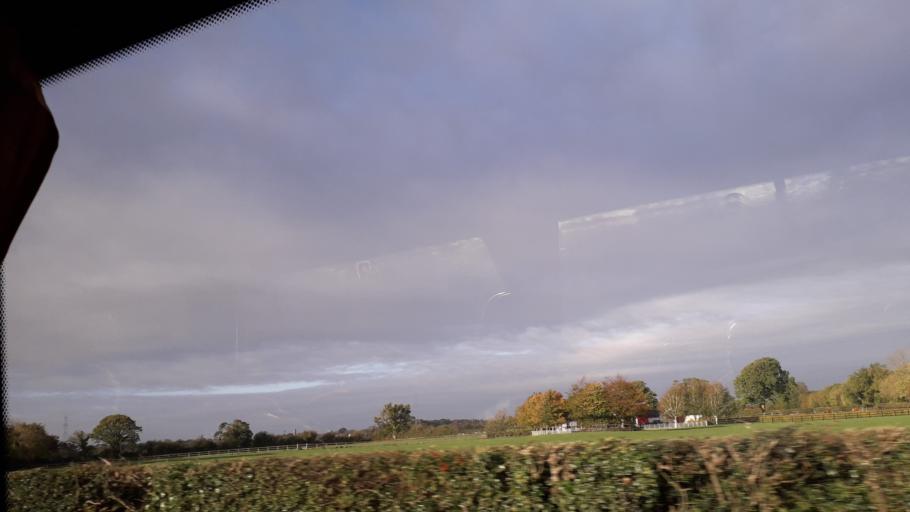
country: IE
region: Leinster
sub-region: Kildare
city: Maynooth
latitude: 53.3567
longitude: -6.5948
